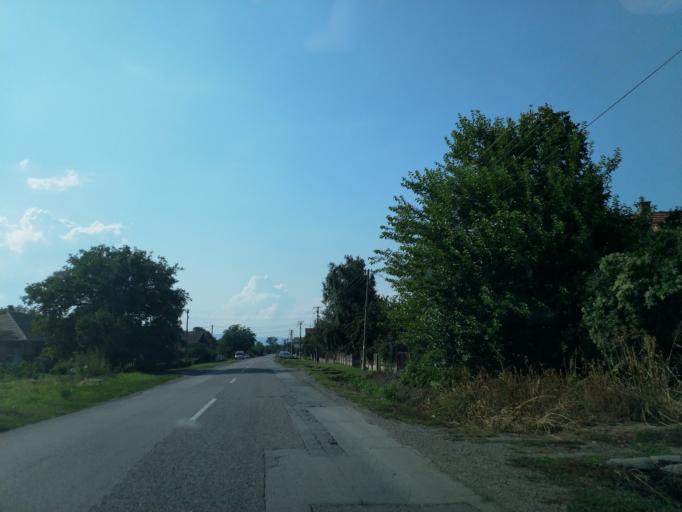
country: RS
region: Central Serbia
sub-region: Rasinski Okrug
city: Cicevac
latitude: 43.7519
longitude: 21.4402
